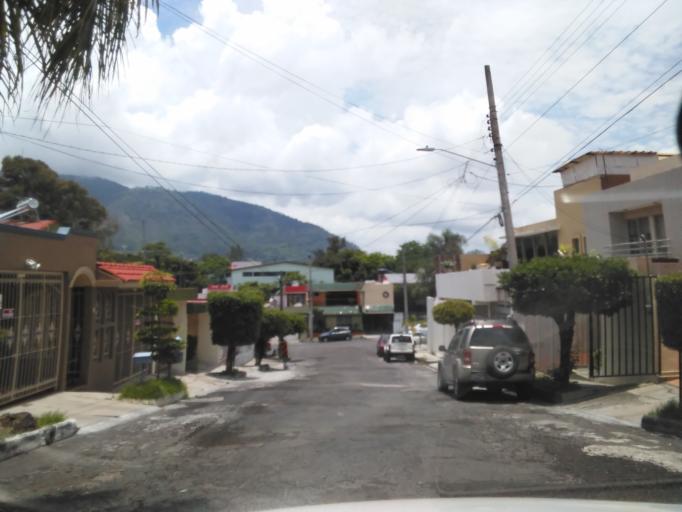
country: MX
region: Nayarit
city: Tepic
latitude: 21.4970
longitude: -104.8986
